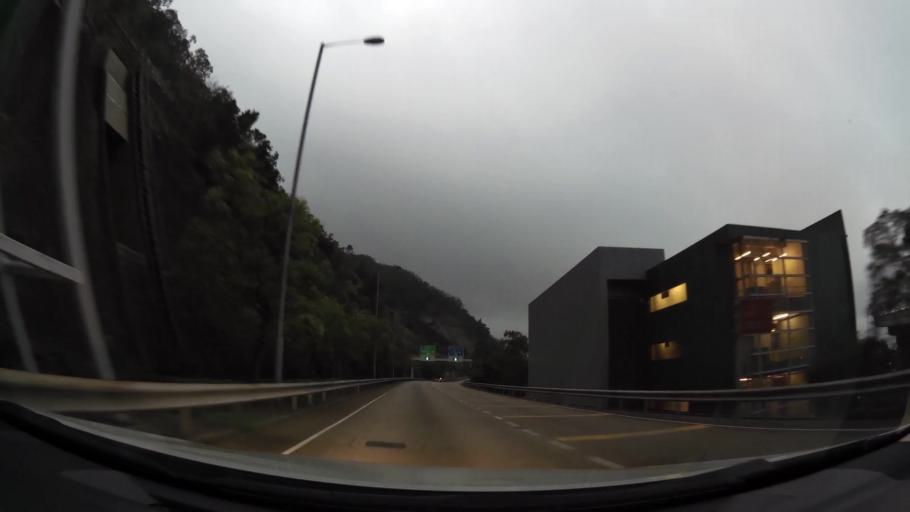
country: HK
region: Tsuen Wan
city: Tsuen Wan
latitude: 22.3548
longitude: 114.0858
